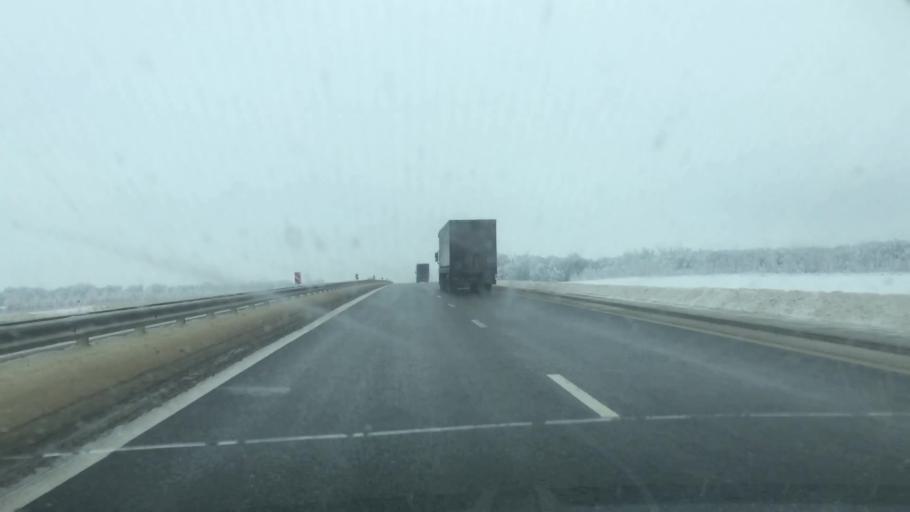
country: RU
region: Lipetsk
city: Stanovoye
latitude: 52.8950
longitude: 38.2314
